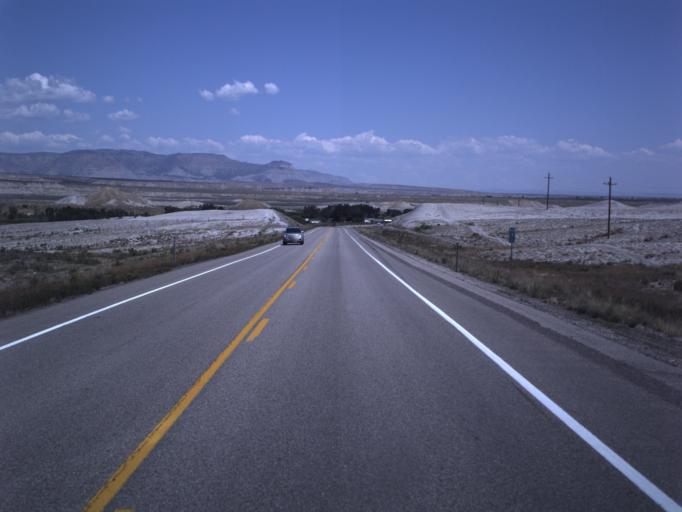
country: US
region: Utah
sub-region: Emery County
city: Ferron
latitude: 39.1400
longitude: -111.0966
